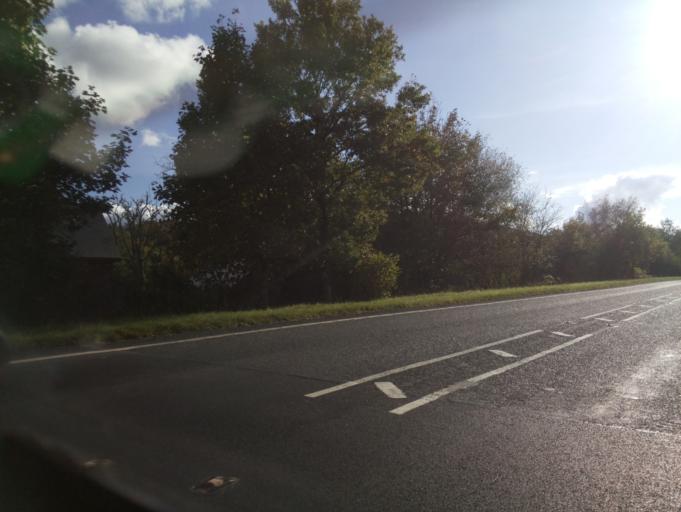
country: GB
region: Wales
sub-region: Sir Powys
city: Brecon
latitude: 51.9766
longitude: -3.3314
